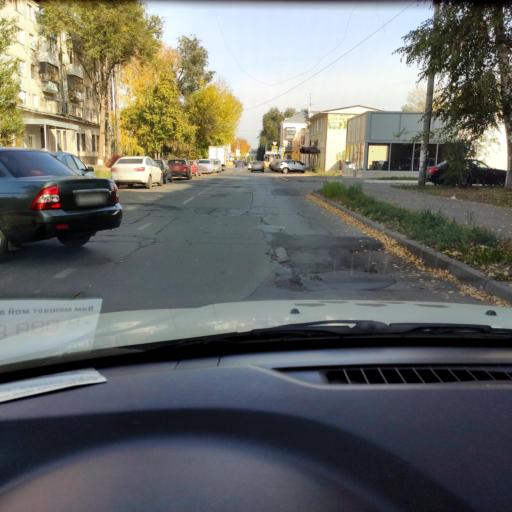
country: RU
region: Samara
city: Tol'yatti
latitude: 53.5210
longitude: 49.4197
